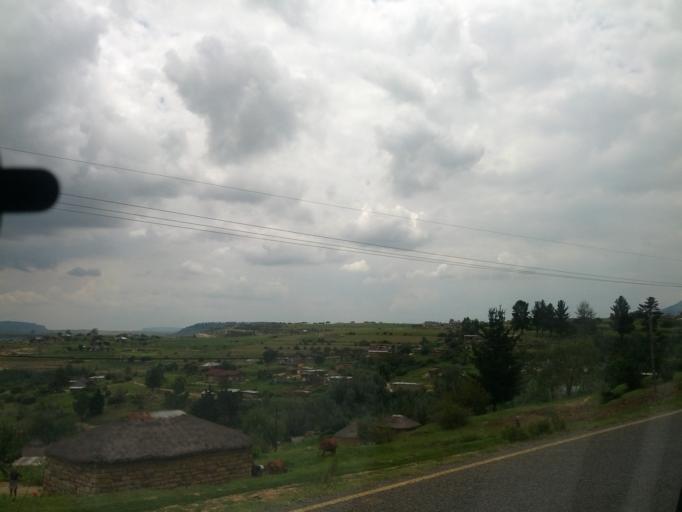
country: LS
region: Leribe
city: Leribe
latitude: -28.9680
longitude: 28.1727
